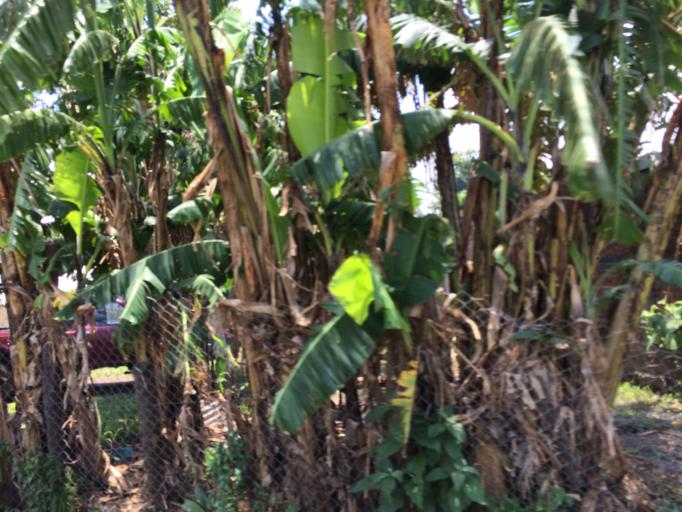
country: MX
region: Michoacan
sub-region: Periban
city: San Francisco Periban
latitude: 19.5572
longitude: -102.3969
